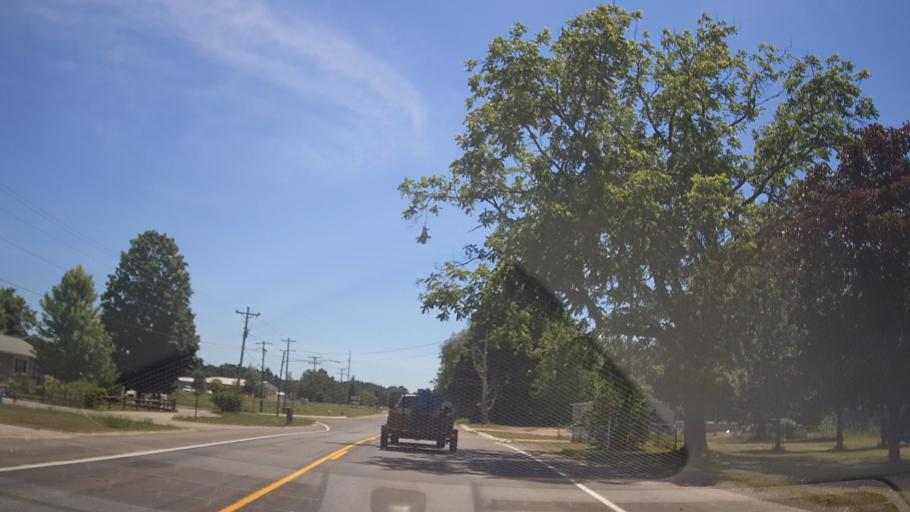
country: US
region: Michigan
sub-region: Grand Traverse County
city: Traverse City
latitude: 44.6586
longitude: -85.6966
